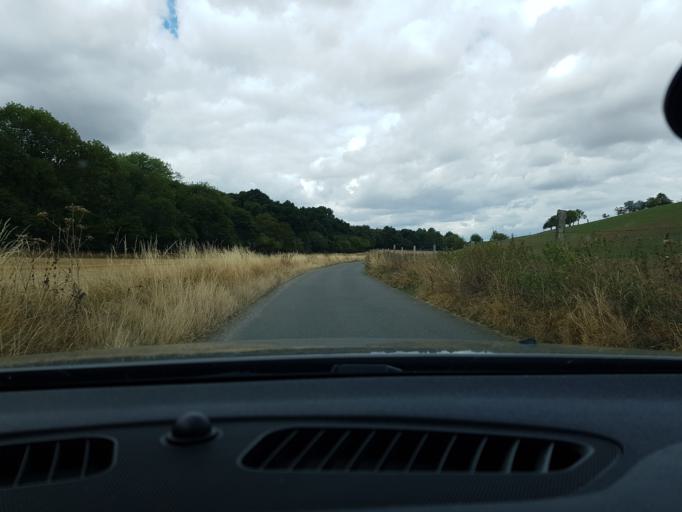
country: GB
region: England
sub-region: West Berkshire
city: Kintbury
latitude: 51.4271
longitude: -1.4746
